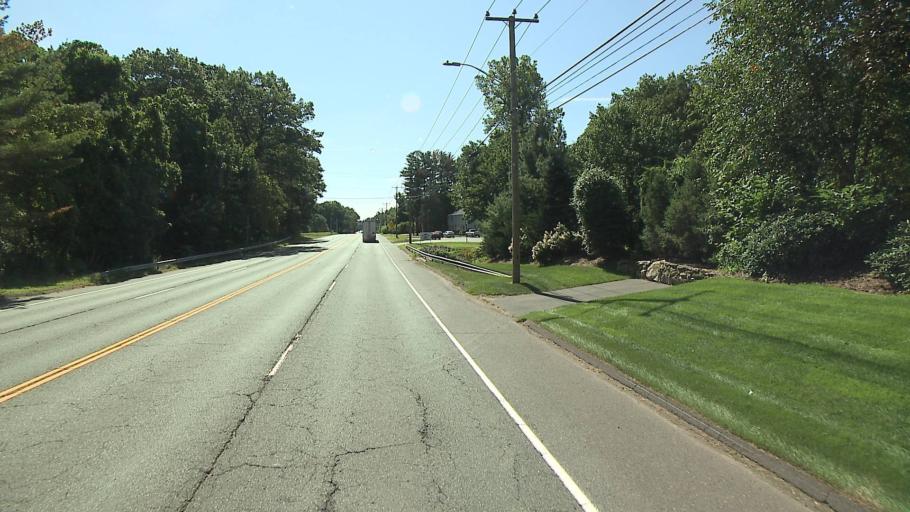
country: US
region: Connecticut
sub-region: Hartford County
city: Blue Hills
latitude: 41.8598
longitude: -72.7113
